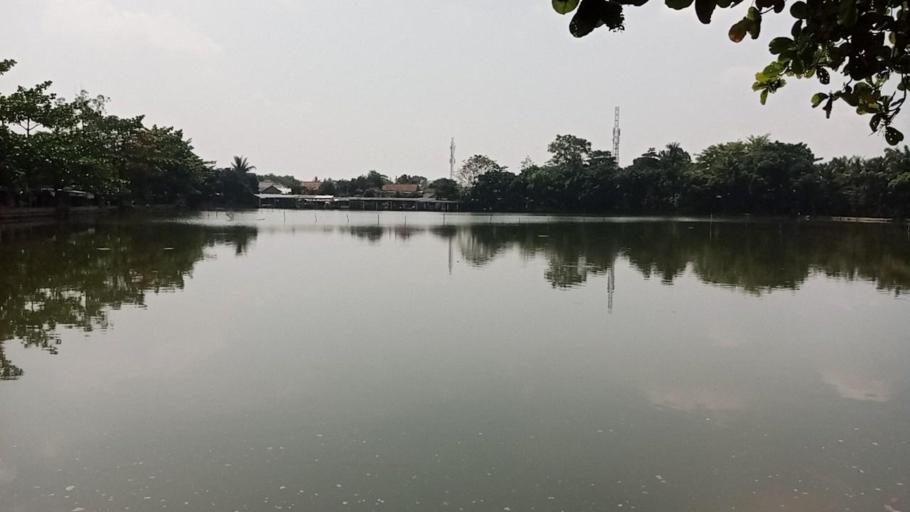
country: ID
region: West Java
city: Parung
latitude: -6.4211
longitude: 106.7480
